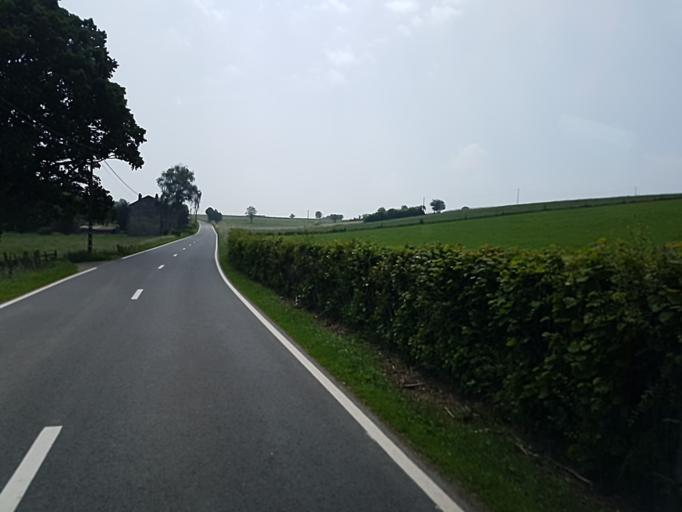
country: BE
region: Wallonia
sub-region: Province du Luxembourg
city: Manhay
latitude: 50.3194
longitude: 5.7301
